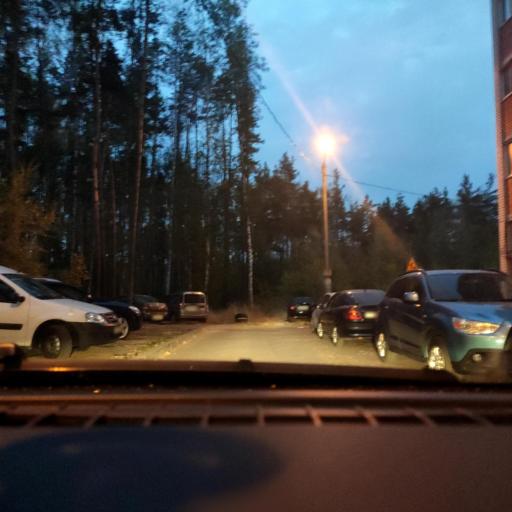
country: RU
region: Voronezj
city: Voronezh
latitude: 51.6941
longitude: 39.2794
